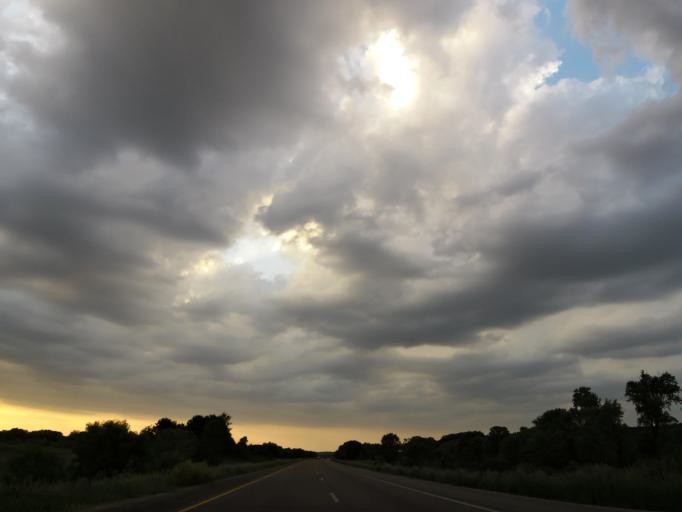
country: US
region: Wisconsin
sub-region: Eau Claire County
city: Fall Creek
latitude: 44.6967
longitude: -91.3393
